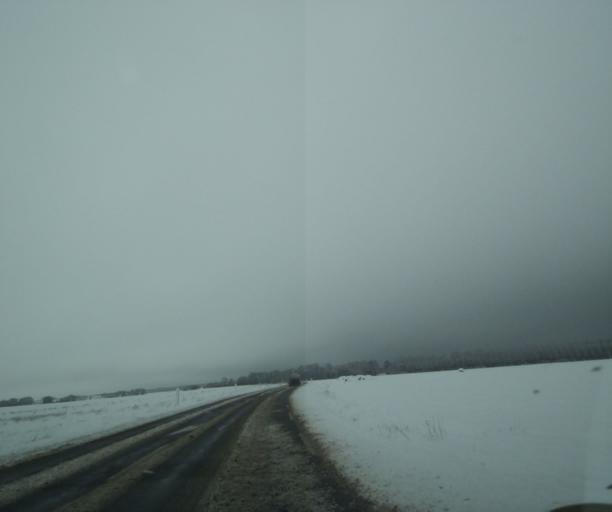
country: FR
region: Champagne-Ardenne
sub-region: Departement de la Haute-Marne
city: Wassy
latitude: 48.5629
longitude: 4.9224
